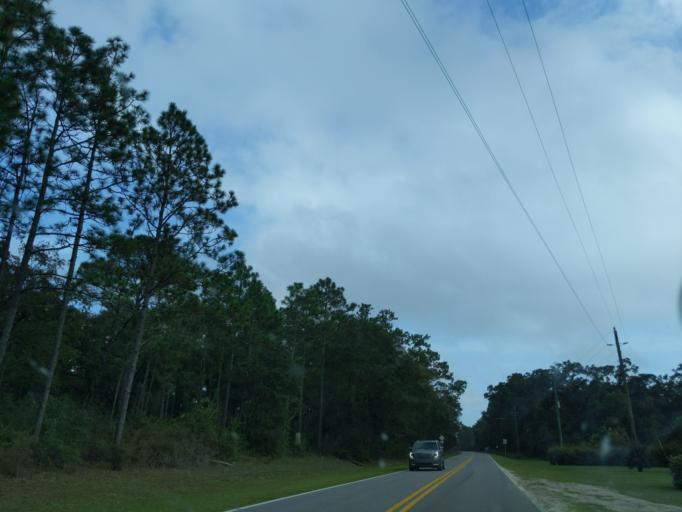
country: US
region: Florida
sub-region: Wakulla County
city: Crawfordville
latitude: 30.1207
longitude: -84.3150
